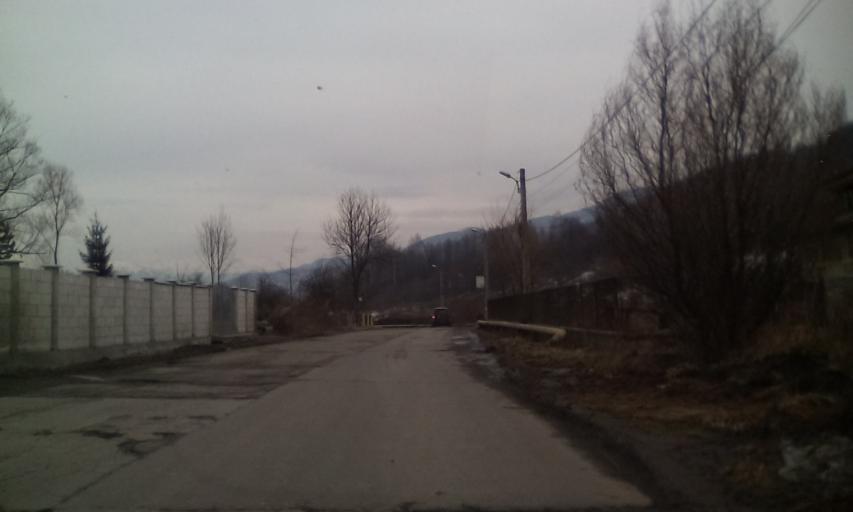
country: RO
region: Hunedoara
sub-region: Comuna Uricani
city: Uricani
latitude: 45.3423
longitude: 23.1716
